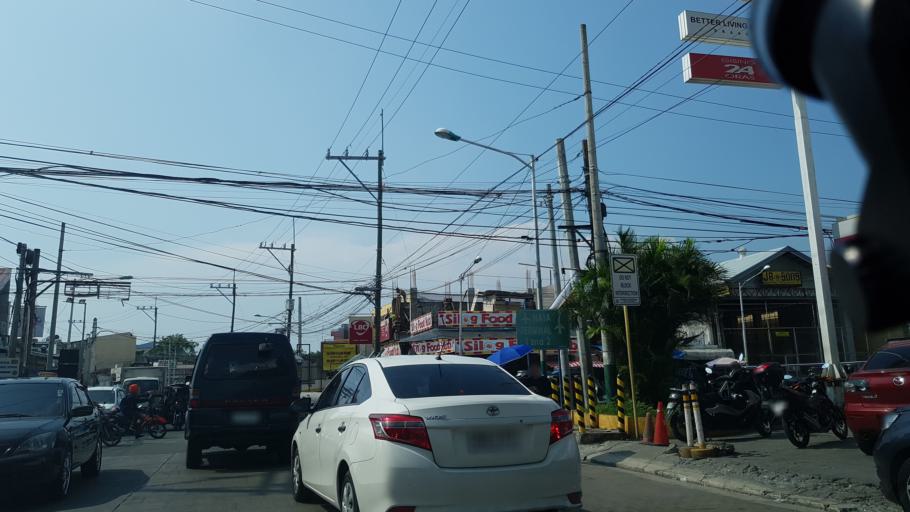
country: PH
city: Sambayanihan People's Village
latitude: 14.4865
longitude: 121.0275
